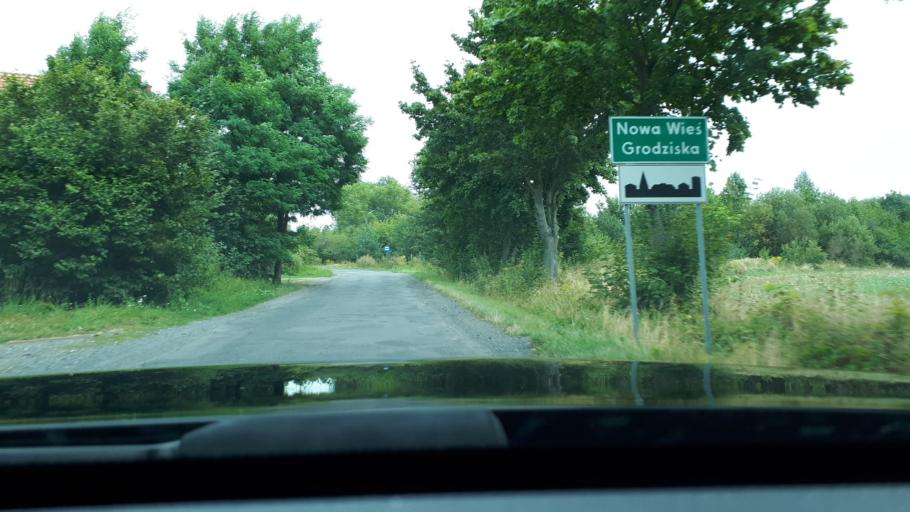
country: PL
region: Lower Silesian Voivodeship
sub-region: Powiat zlotoryjski
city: Olszanica
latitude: 51.1403
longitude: 15.7359
